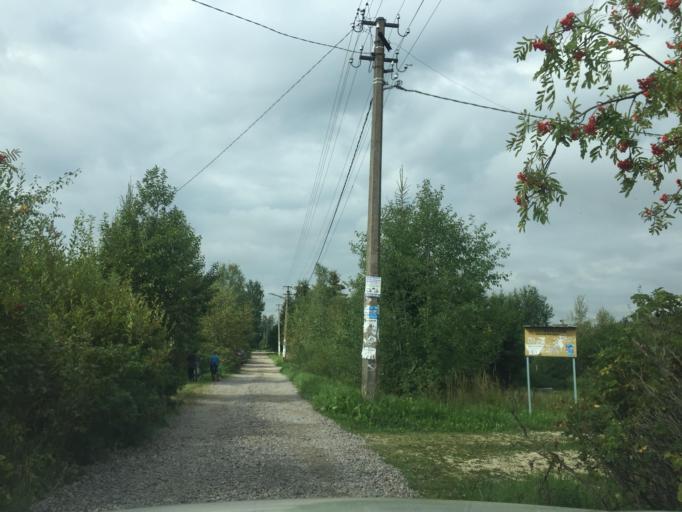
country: RU
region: Leningrad
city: Siverskiy
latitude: 59.2963
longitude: 30.0295
